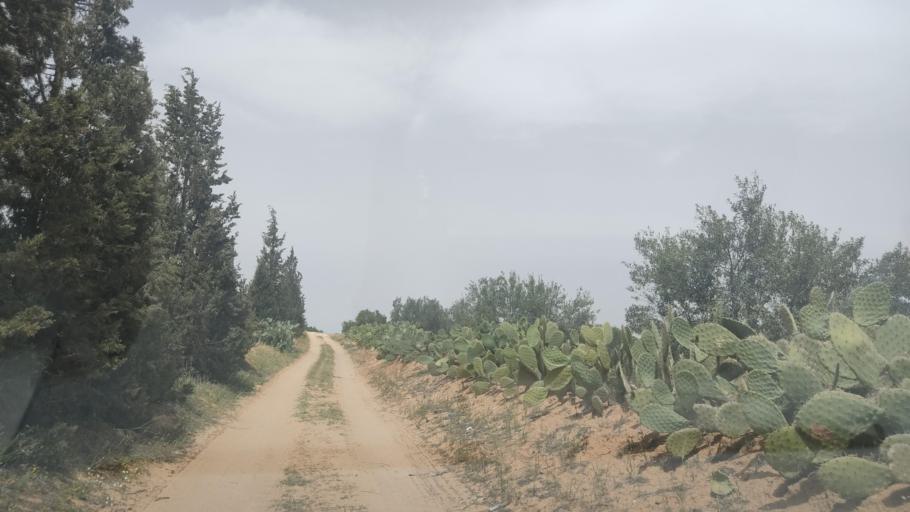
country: TN
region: Safaqis
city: Sfax
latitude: 34.8411
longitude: 10.5938
